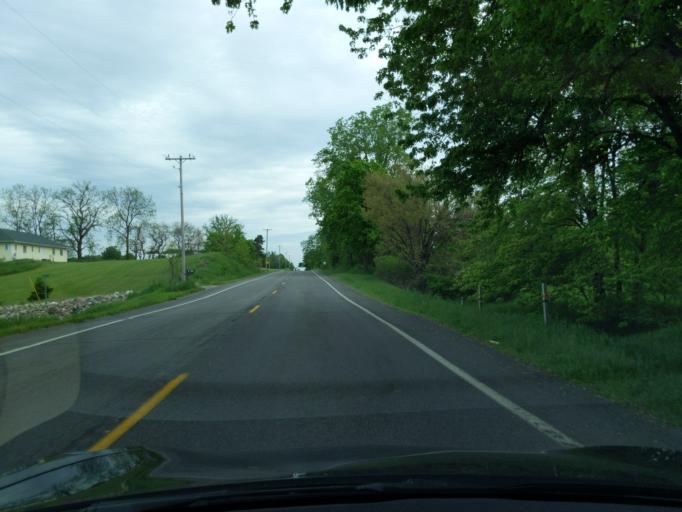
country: US
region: Michigan
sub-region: Ingham County
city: Mason
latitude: 42.5641
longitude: -84.3569
